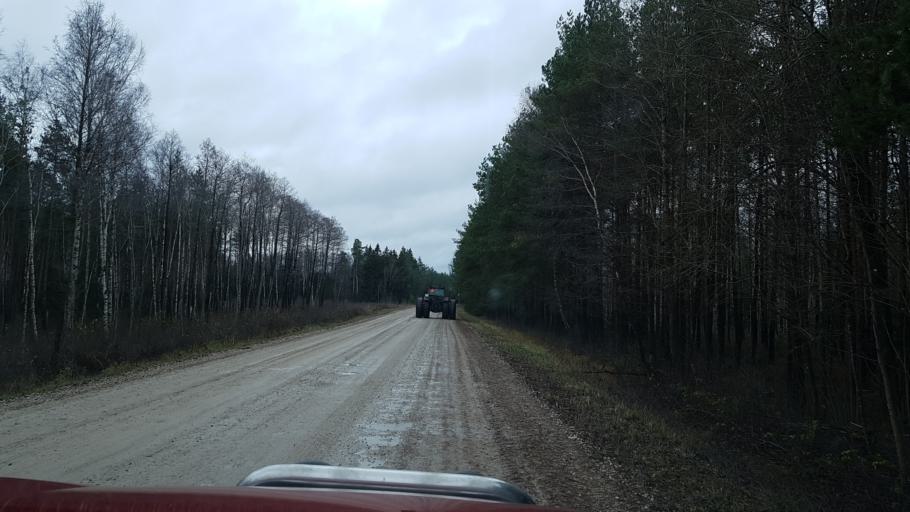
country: EE
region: Paernumaa
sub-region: Halinga vald
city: Parnu-Jaagupi
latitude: 58.5484
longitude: 24.4120
